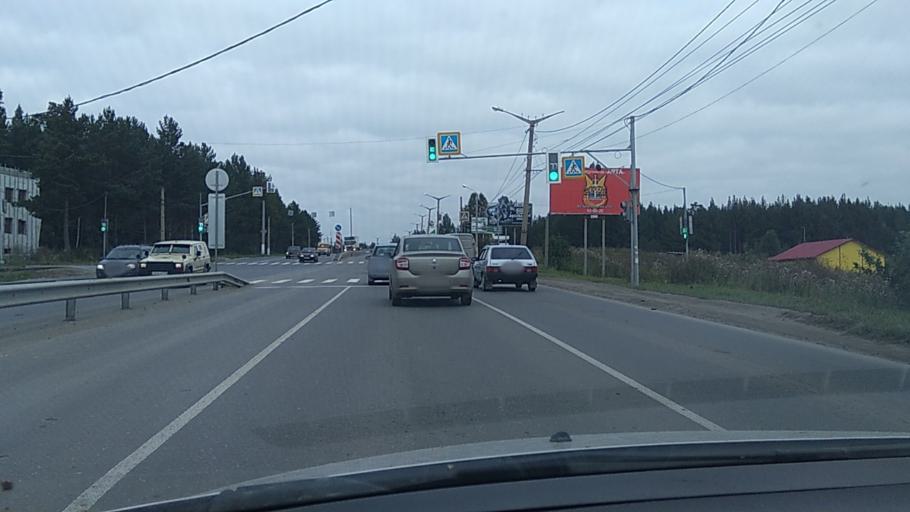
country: RU
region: Chelyabinsk
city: Zlatoust
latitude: 55.1219
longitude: 59.6970
